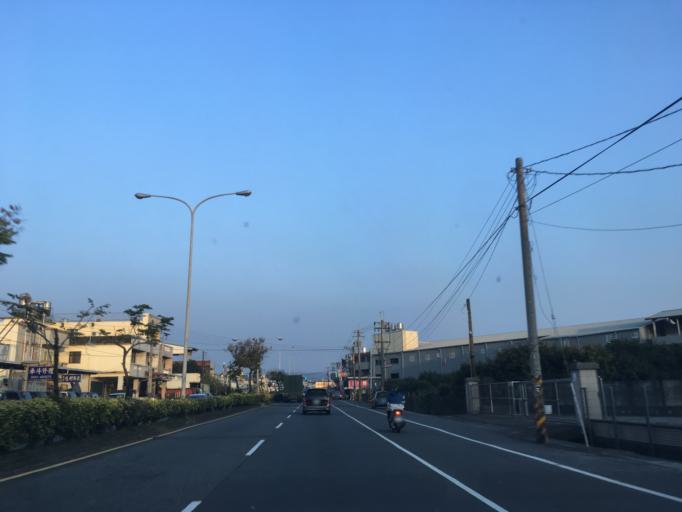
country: TW
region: Taiwan
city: Zhongxing New Village
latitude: 24.0022
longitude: 120.6562
